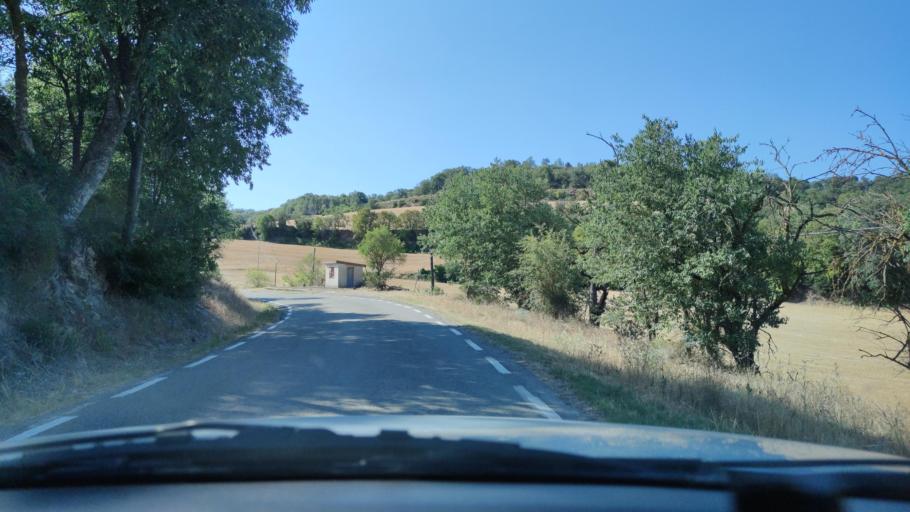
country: ES
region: Catalonia
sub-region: Provincia de Lleida
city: Ivorra
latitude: 41.7375
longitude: 1.3520
